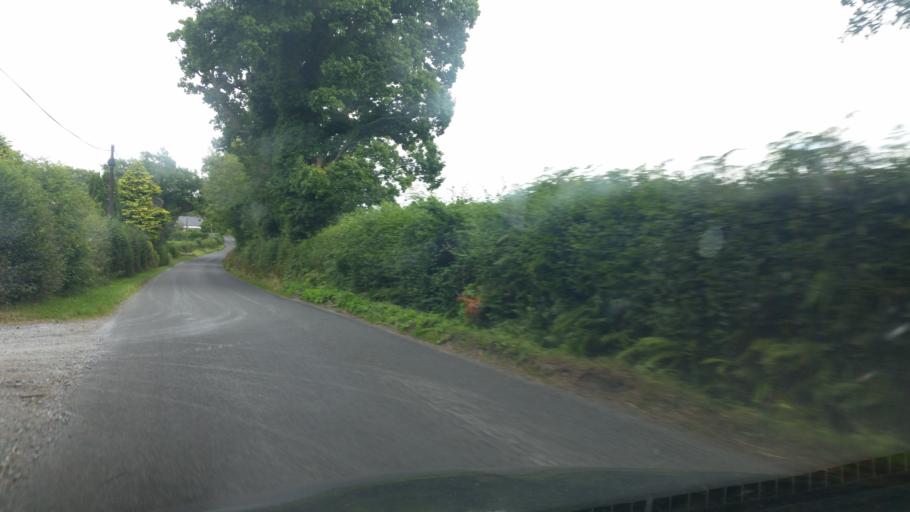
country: IE
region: Leinster
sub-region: Loch Garman
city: Bunclody
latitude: 52.6526
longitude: -6.6712
